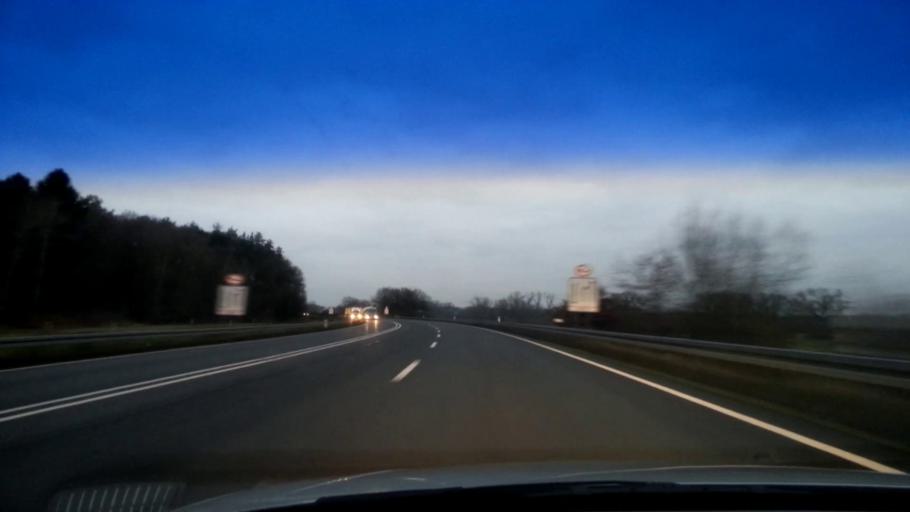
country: DE
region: Bavaria
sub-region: Upper Franconia
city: Hirschaid
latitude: 49.8156
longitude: 10.9645
